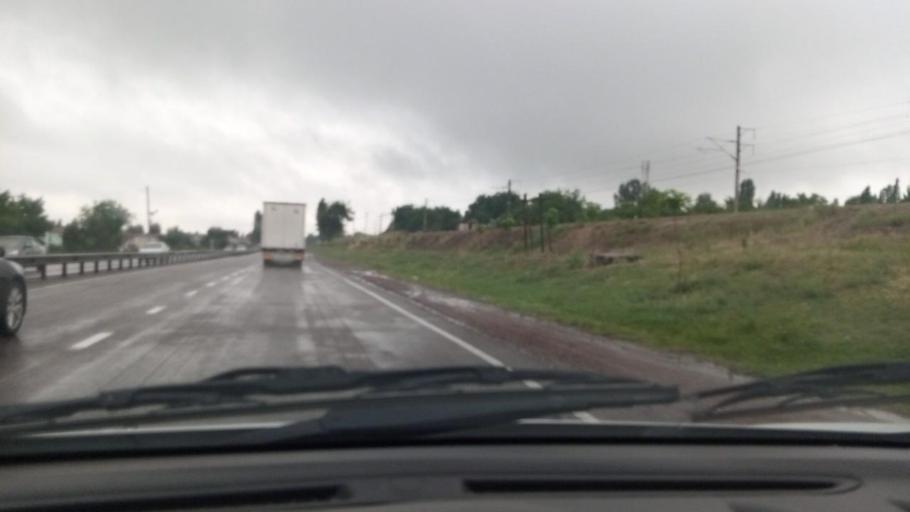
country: UZ
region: Toshkent
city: Ohangaron
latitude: 40.8991
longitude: 69.6934
